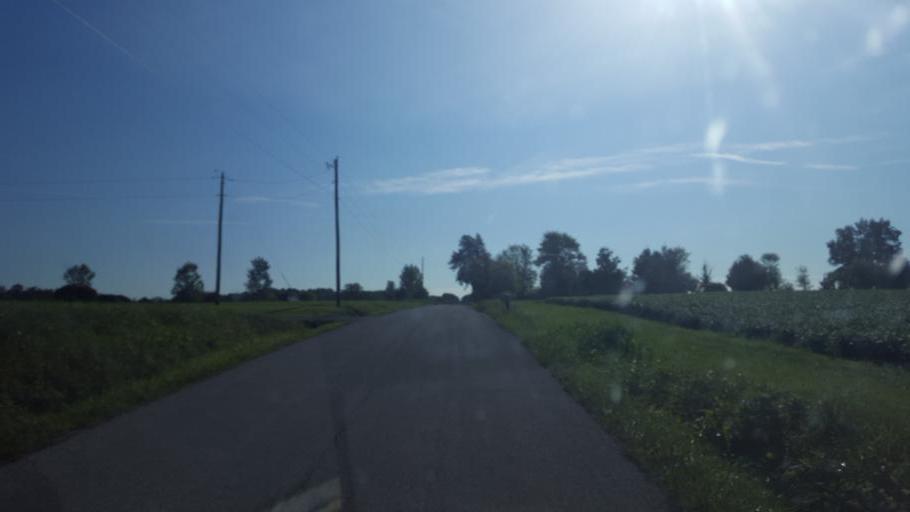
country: US
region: Ohio
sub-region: Richland County
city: Lexington
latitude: 40.6446
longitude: -82.5992
